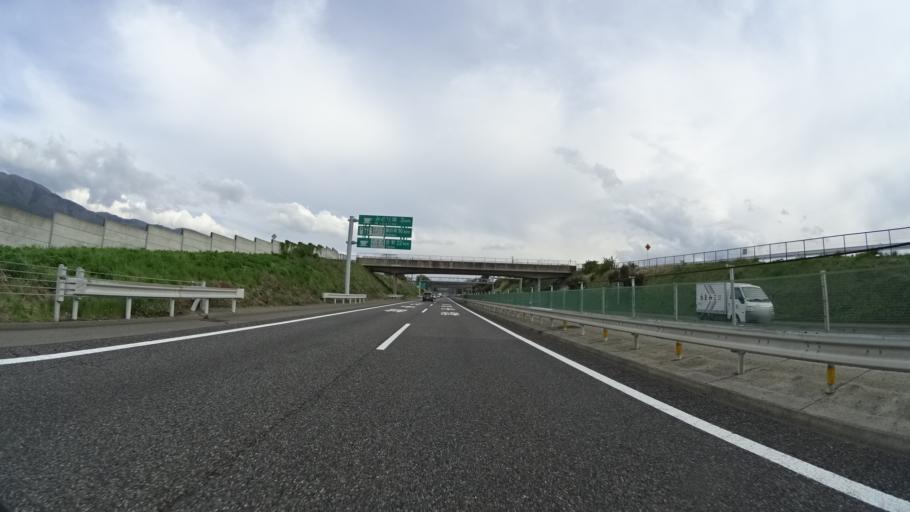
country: JP
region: Nagano
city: Shiojiri
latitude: 36.1277
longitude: 137.9754
